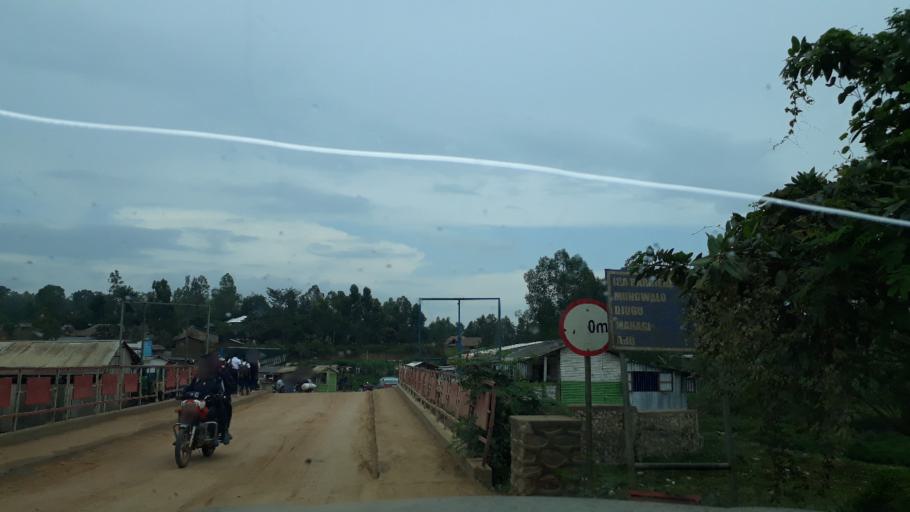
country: CD
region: Eastern Province
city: Bunia
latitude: 1.5773
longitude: 30.2491
